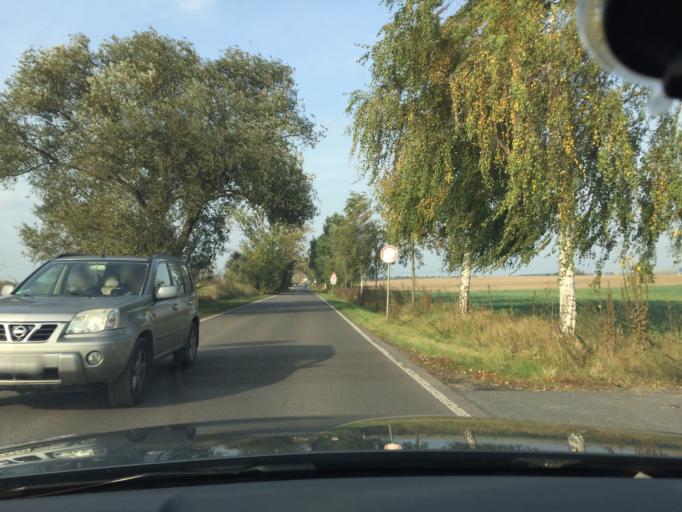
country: DE
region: Berlin
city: Buch
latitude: 52.6100
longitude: 13.5214
